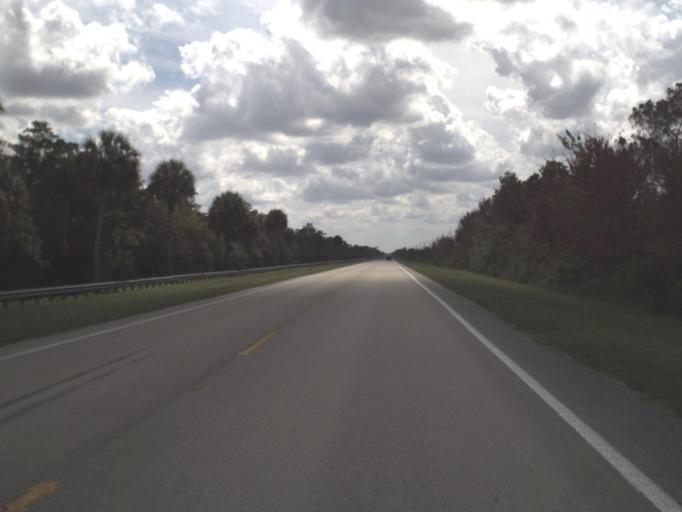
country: US
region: Florida
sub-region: Collier County
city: Orangetree
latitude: 26.1094
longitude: -81.3448
